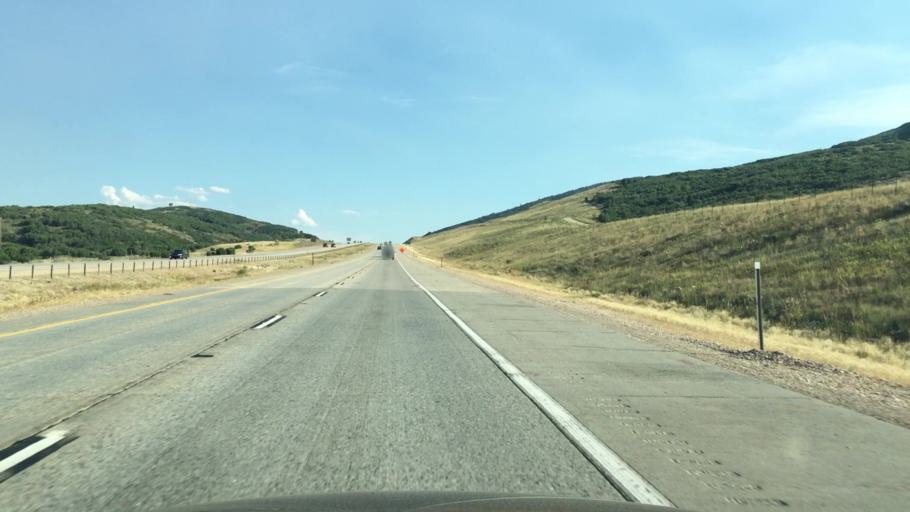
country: US
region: Utah
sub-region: Summit County
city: Park City
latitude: 40.6683
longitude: -111.4597
